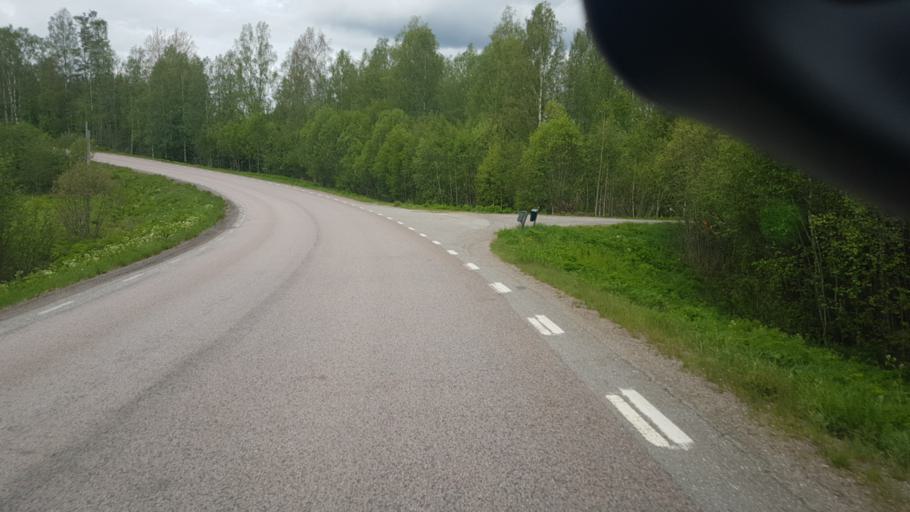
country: SE
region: Vaermland
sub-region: Eda Kommun
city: Amotfors
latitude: 59.8672
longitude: 12.4496
